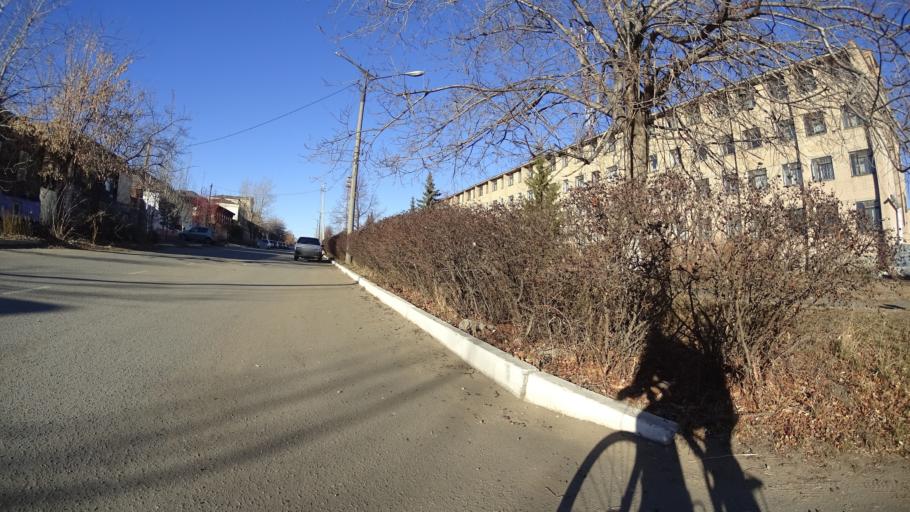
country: RU
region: Chelyabinsk
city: Troitsk
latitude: 54.0803
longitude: 61.5625
